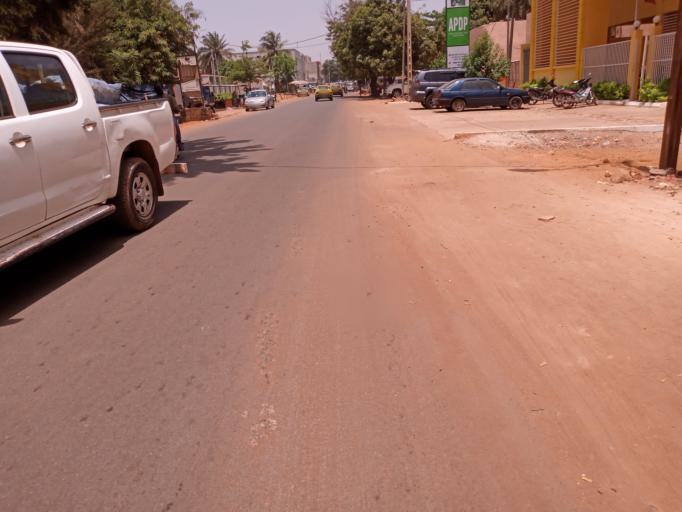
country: ML
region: Bamako
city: Bamako
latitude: 12.6353
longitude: -8.0008
